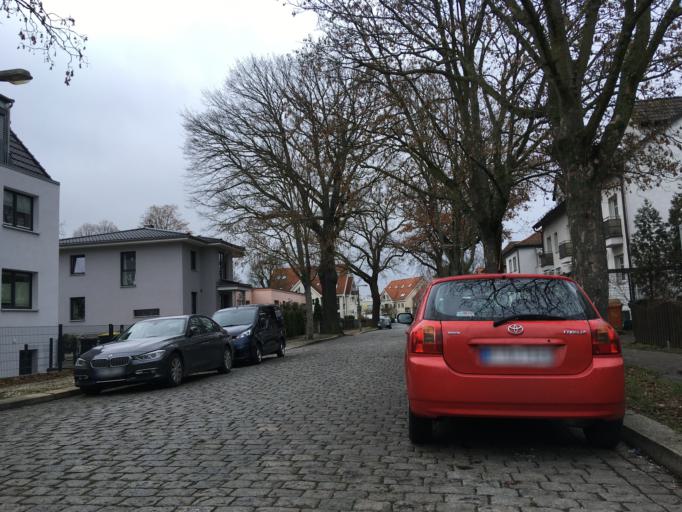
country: DE
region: Berlin
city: Wilhelmsruh
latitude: 52.5838
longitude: 13.3795
